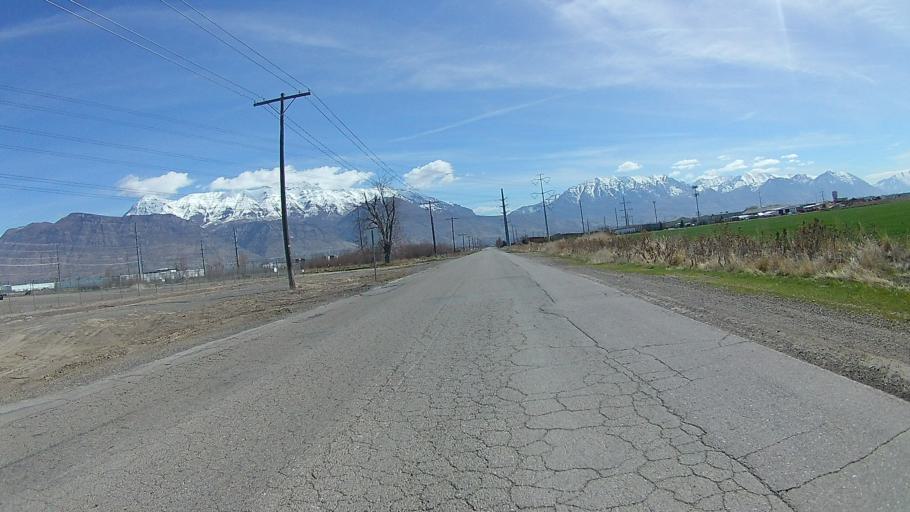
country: US
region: Utah
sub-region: Utah County
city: American Fork
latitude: 40.3477
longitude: -111.7895
